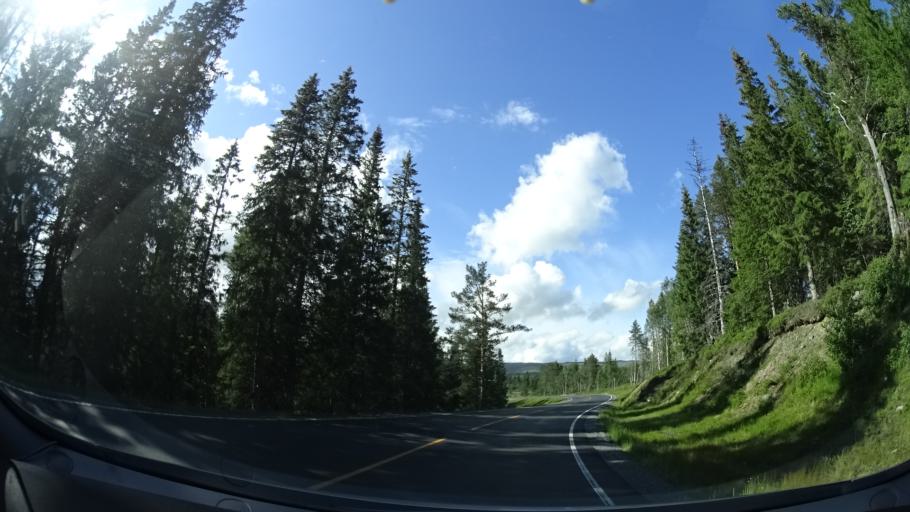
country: NO
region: Sor-Trondelag
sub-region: Snillfjord
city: Krokstadora
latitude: 63.2327
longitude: 9.5610
